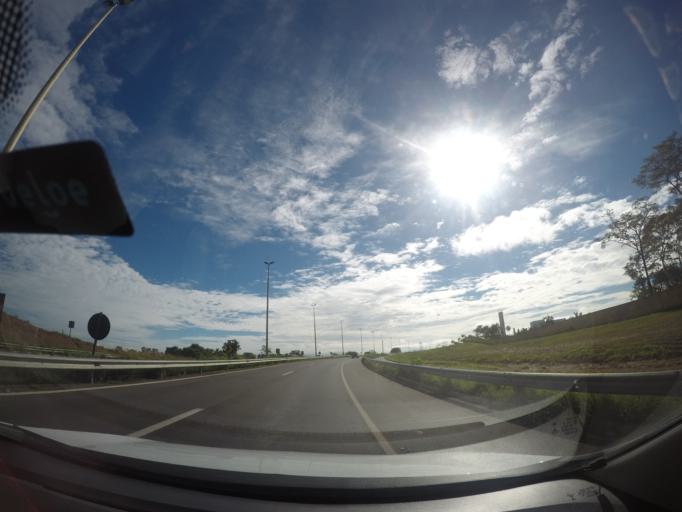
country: BR
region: Goias
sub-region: Senador Canedo
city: Senador Canedo
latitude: -16.6863
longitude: -49.1637
